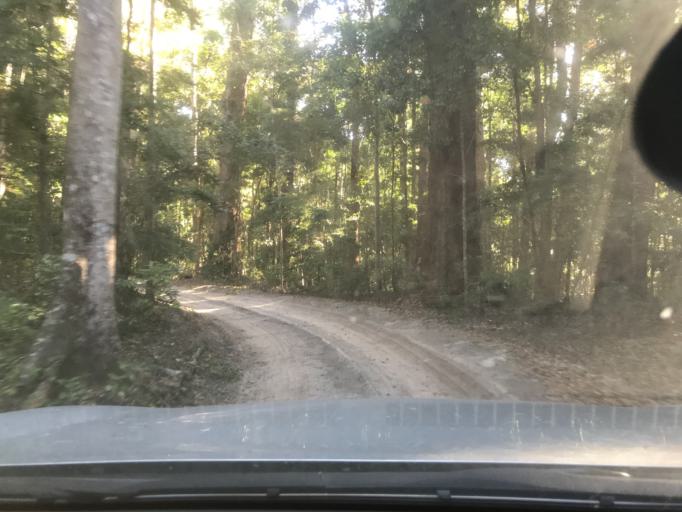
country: AU
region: Queensland
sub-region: Fraser Coast
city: Urangan
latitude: -25.3241
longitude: 153.1529
